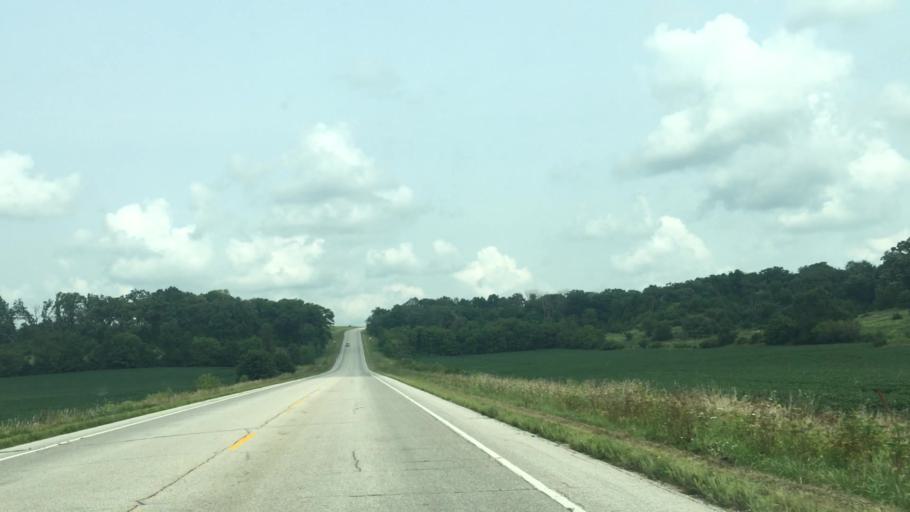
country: US
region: Minnesota
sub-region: Fillmore County
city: Harmony
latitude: 43.6347
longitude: -91.9299
